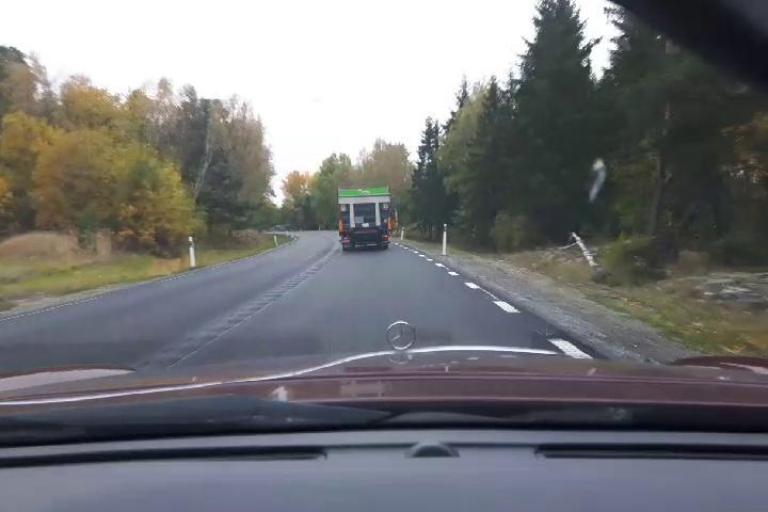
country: SE
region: Soedermanland
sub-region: Strangnas Kommun
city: Strangnas
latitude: 59.4234
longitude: 17.0255
